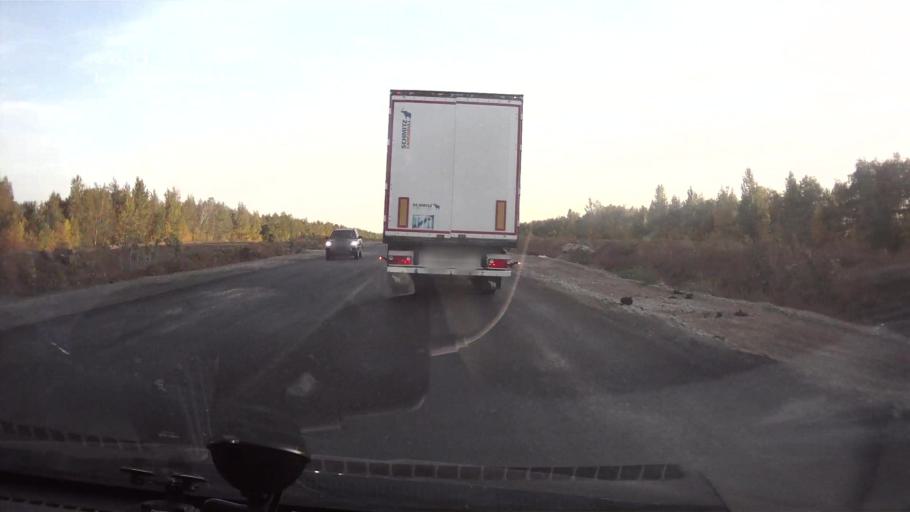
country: RU
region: Saratov
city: Krasnoarmeysk
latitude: 51.0193
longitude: 45.6209
